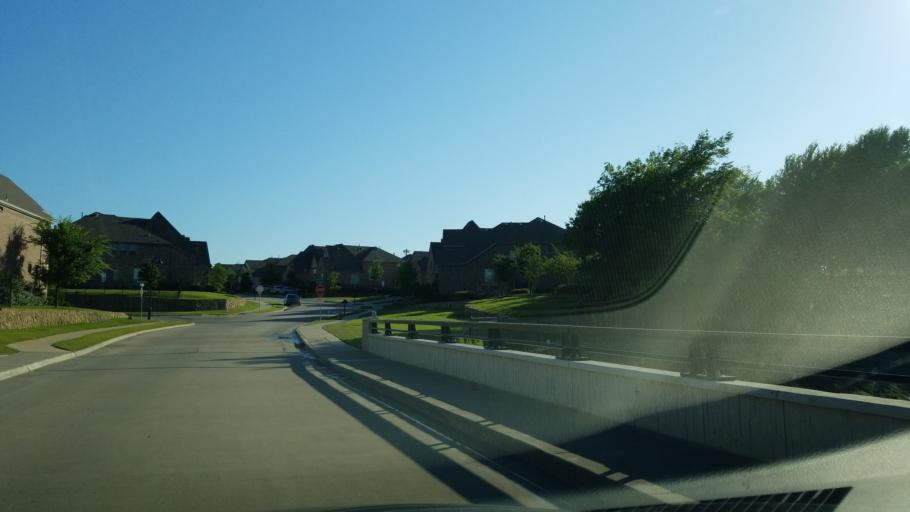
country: US
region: Texas
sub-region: Dallas County
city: Coppell
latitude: 32.9093
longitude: -96.9882
